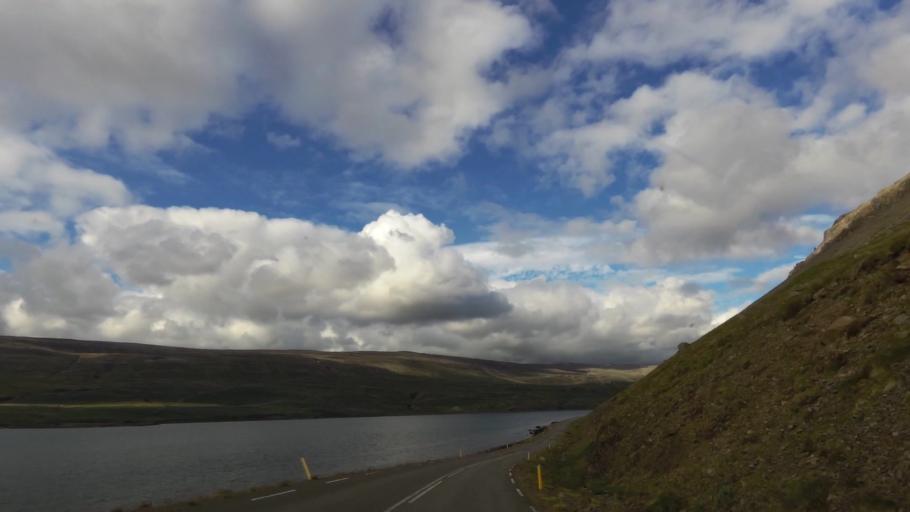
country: IS
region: West
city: Olafsvik
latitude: 65.5254
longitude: -23.8229
